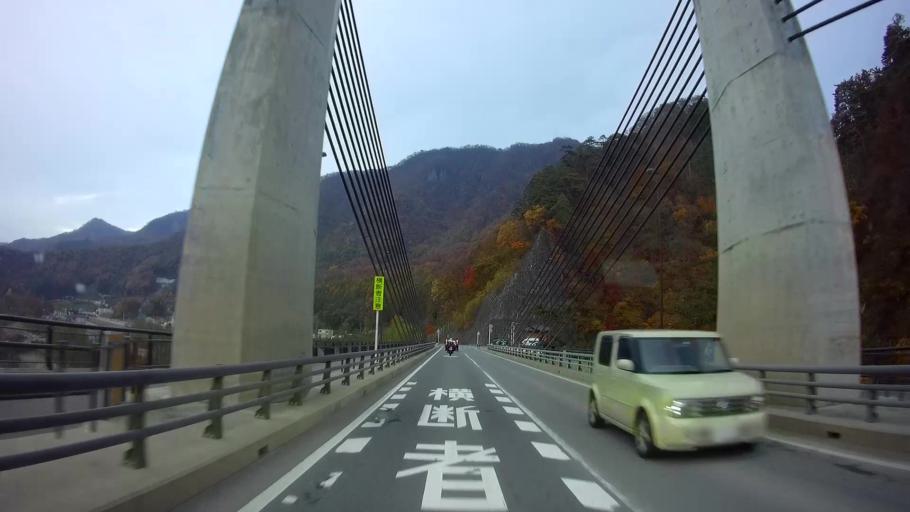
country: JP
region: Gunma
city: Nakanojomachi
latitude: 36.5444
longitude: 138.6892
